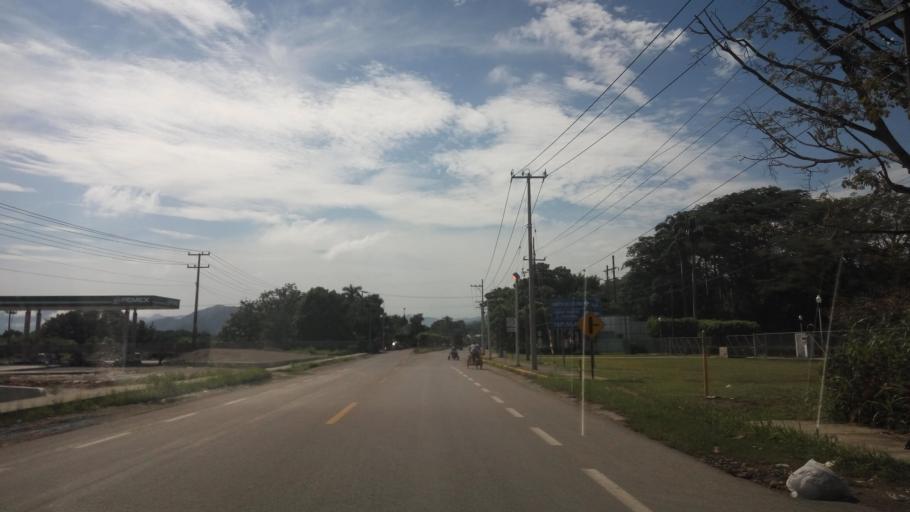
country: MX
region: Tabasco
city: Teapa
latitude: 17.5715
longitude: -92.9566
